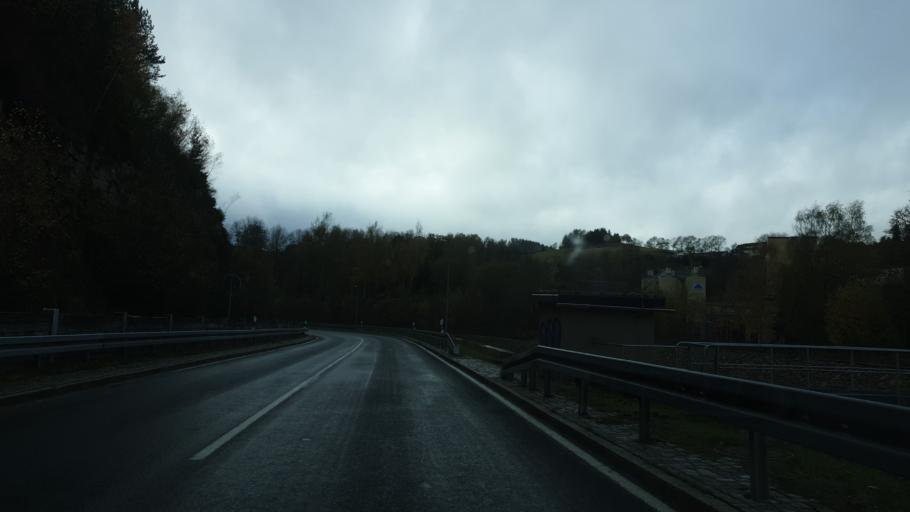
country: DE
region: Saxony
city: Schoenheide
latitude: 50.5038
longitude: 12.5551
